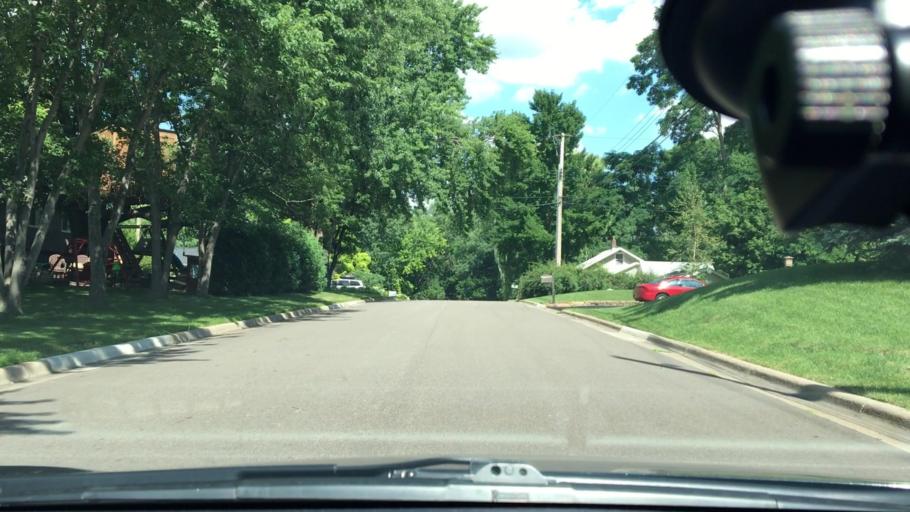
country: US
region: Minnesota
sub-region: Hennepin County
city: Golden Valley
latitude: 44.9945
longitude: -93.3887
